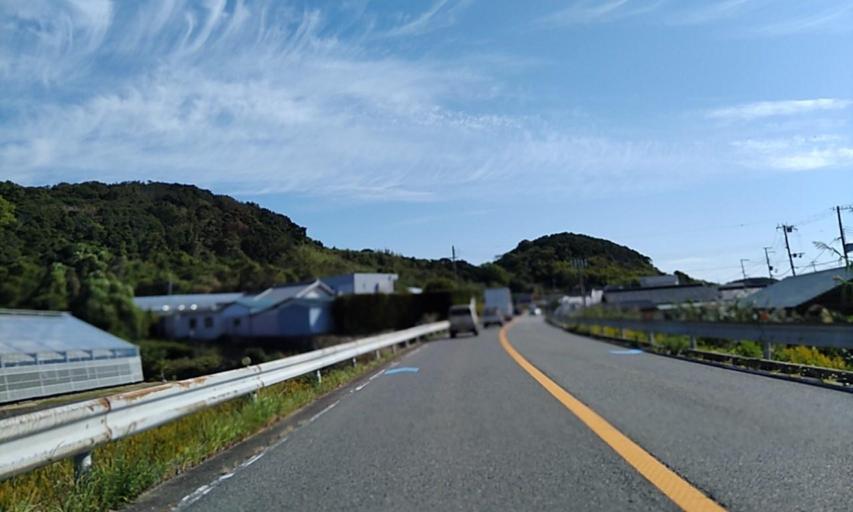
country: JP
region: Wakayama
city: Gobo
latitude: 33.8542
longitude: 135.1660
